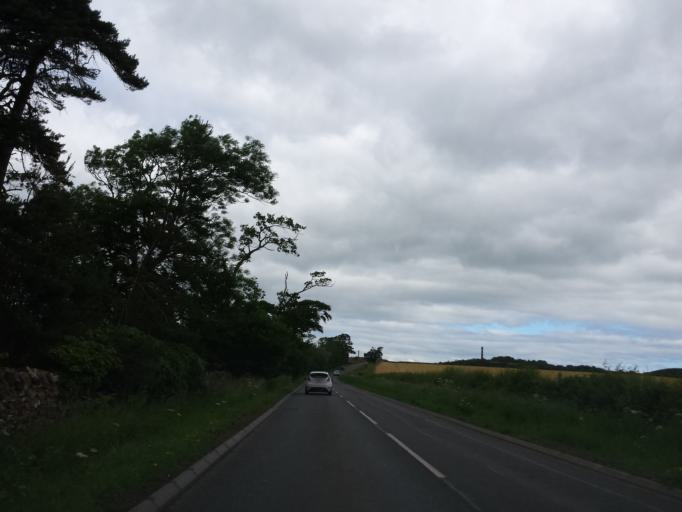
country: GB
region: Scotland
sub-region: East Lothian
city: Haddington
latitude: 55.9649
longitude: -2.7950
